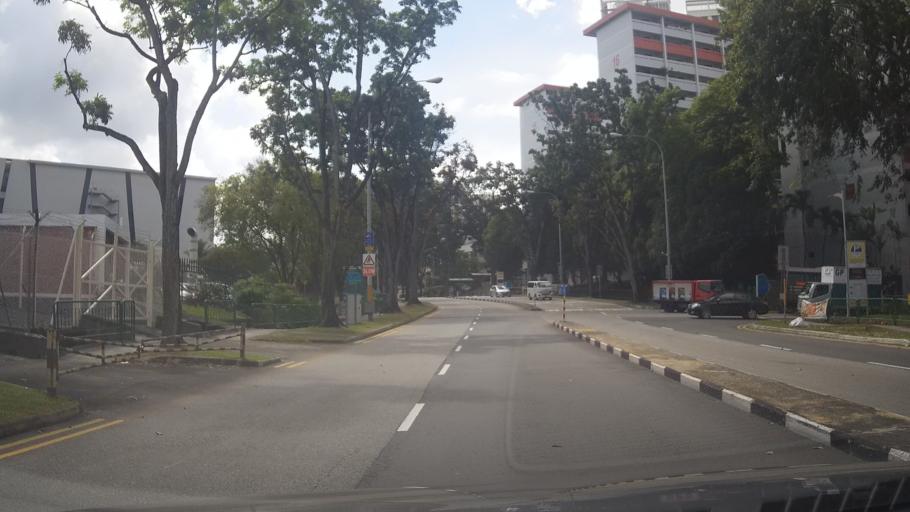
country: MY
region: Johor
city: Johor Bahru
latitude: 1.4435
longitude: 103.7780
